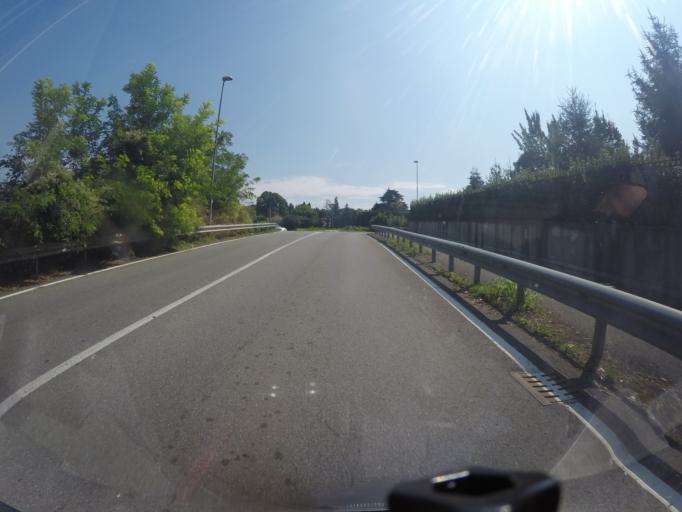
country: IT
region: Lombardy
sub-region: Provincia di Lecco
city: Canova-San Zeno
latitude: 45.7110
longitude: 9.4053
